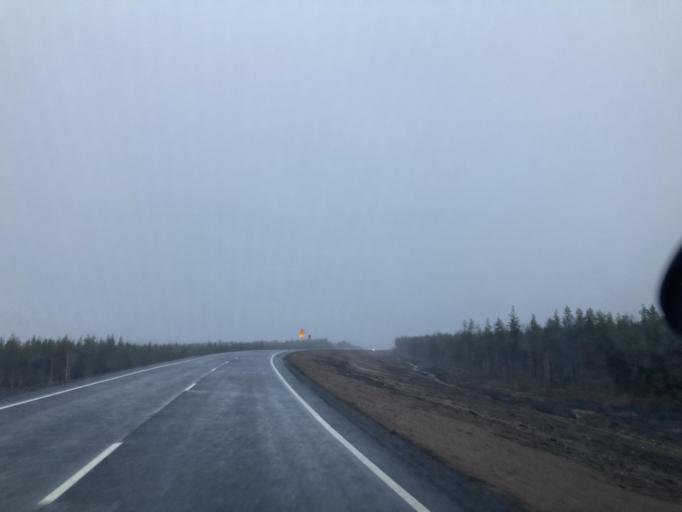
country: FI
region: Lapland
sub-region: Rovaniemi
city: Rovaniemi
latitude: 66.5874
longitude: 25.8008
